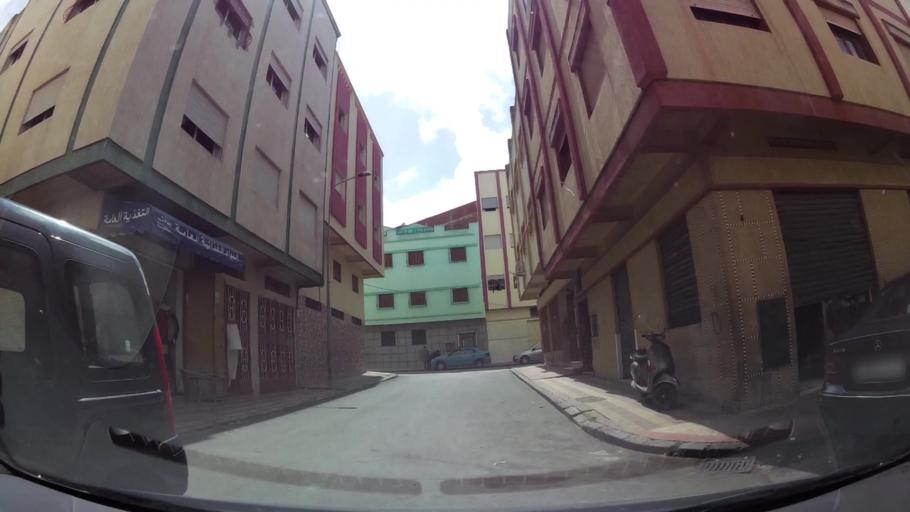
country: MA
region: Tanger-Tetouan
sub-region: Tanger-Assilah
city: Tangier
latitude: 35.7569
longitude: -5.8177
